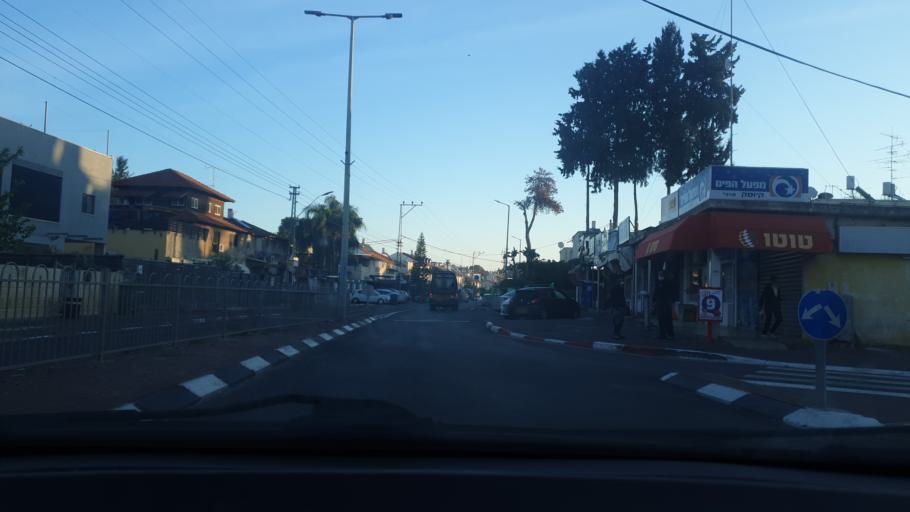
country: IL
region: Central District
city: Ramla
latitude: 31.9347
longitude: 34.8630
